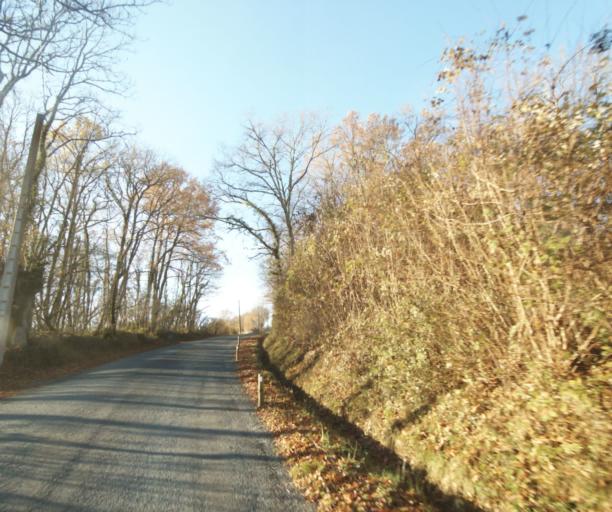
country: FR
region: Poitou-Charentes
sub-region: Departement de la Charente-Maritime
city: Fontcouverte
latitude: 45.7699
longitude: -0.6058
